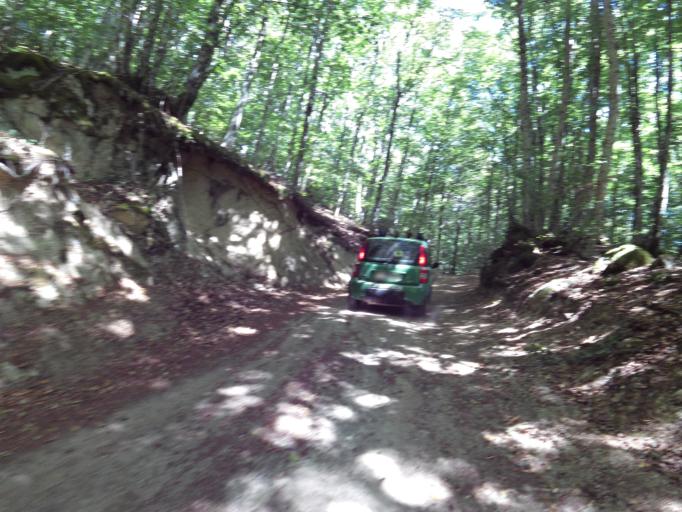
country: IT
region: Calabria
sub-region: Provincia di Vibo-Valentia
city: Mongiana
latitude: 38.5188
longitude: 16.3452
